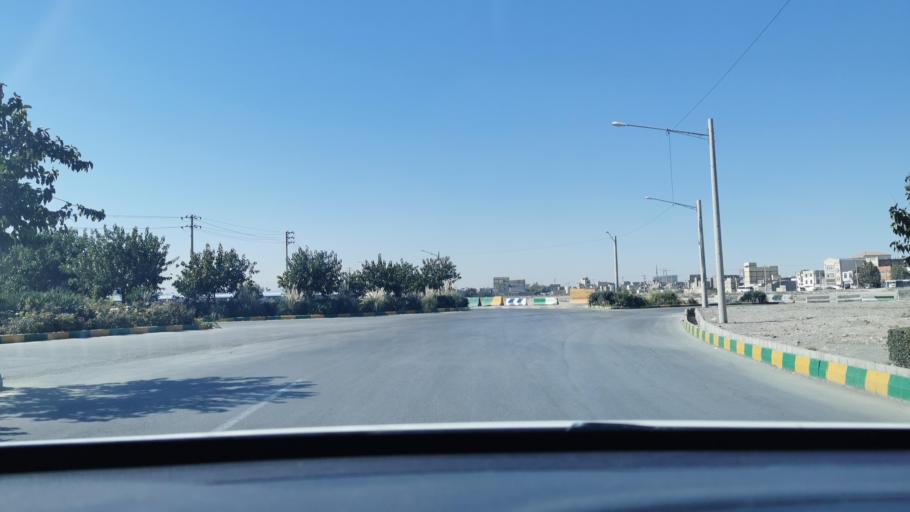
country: IR
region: Razavi Khorasan
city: Mashhad
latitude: 36.3359
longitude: 59.6235
